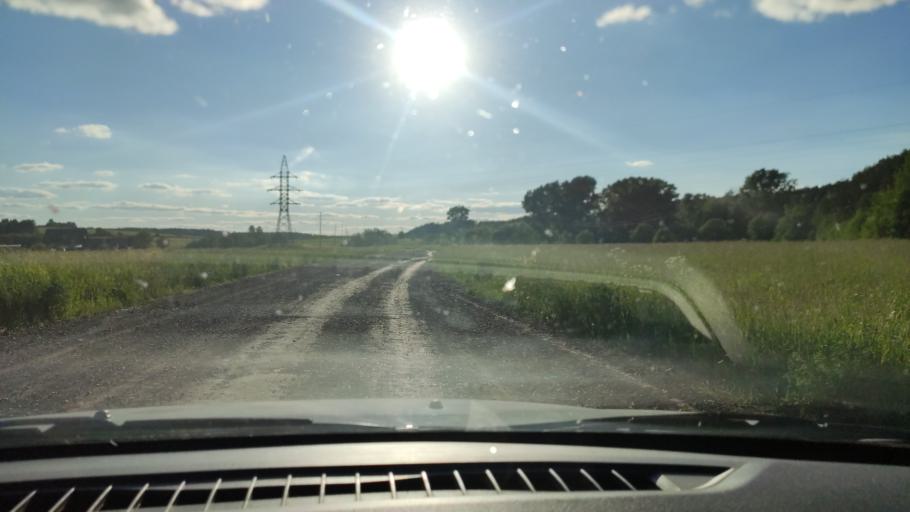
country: RU
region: Perm
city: Orda
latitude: 57.3006
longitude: 56.6216
